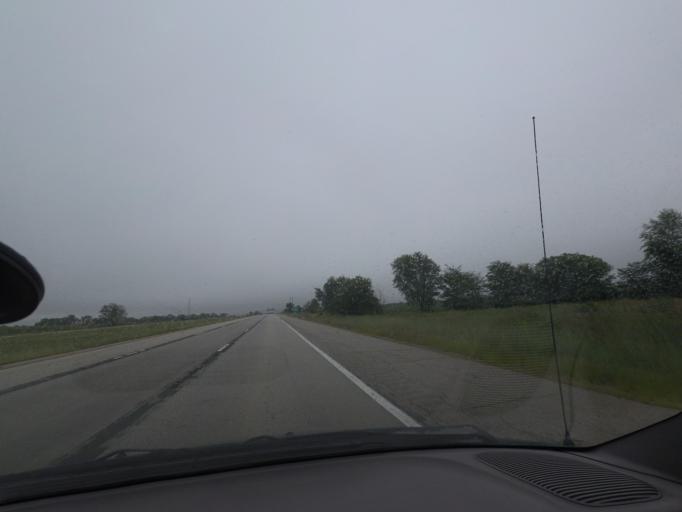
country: US
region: Illinois
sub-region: Macon County
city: Harristown
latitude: 39.8346
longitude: -89.0652
